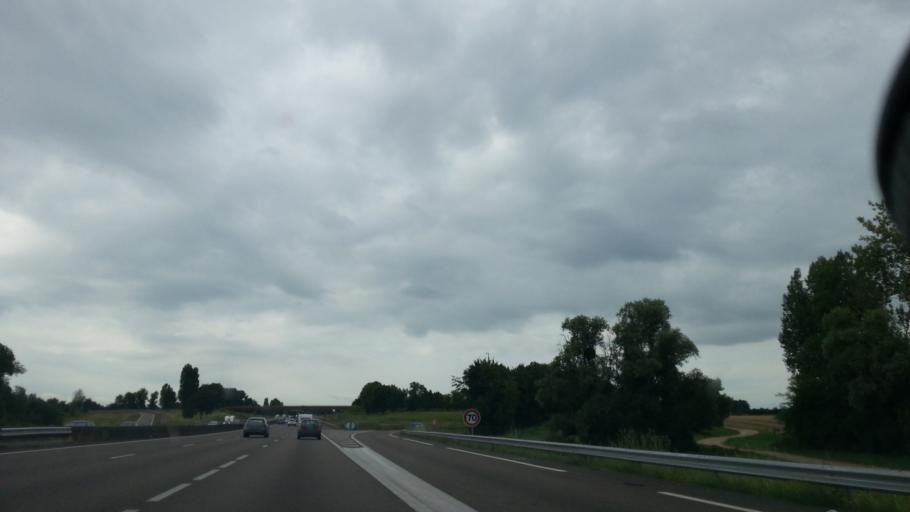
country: FR
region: Bourgogne
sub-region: Departement de Saone-et-Loire
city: Champforgeuil
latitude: 46.8080
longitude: 4.8263
